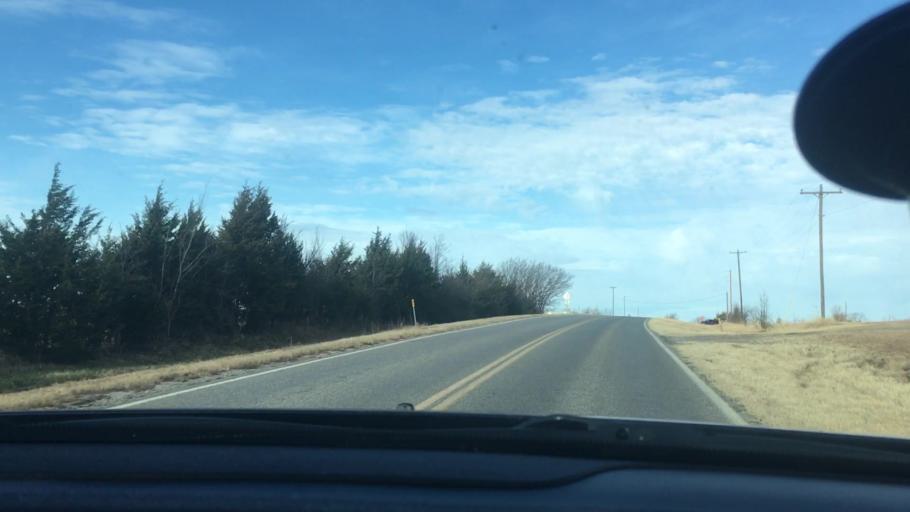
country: US
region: Oklahoma
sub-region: Seminole County
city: Konawa
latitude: 34.9697
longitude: -96.7761
